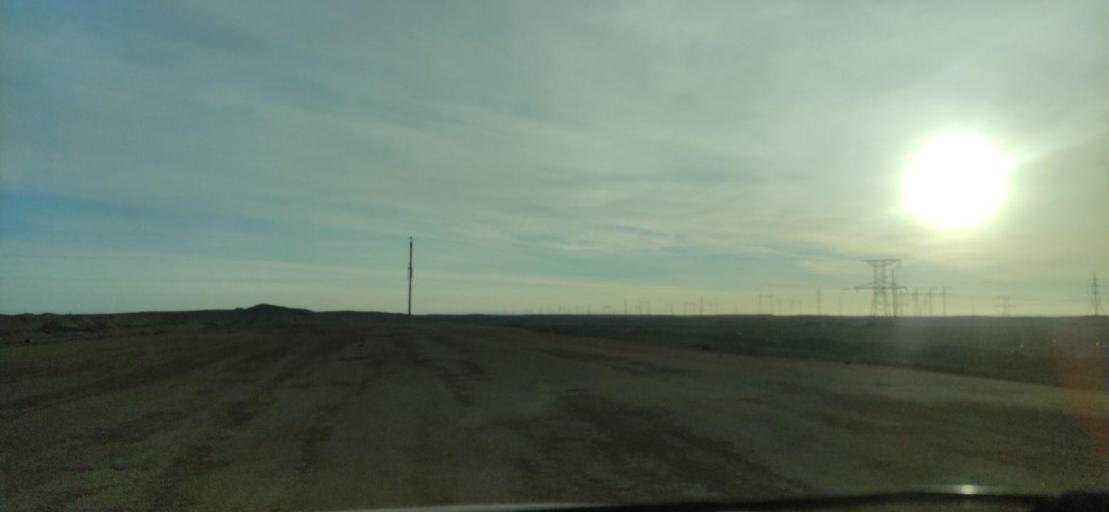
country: KZ
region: Qaraghandy
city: Saryshaghan
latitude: 46.1223
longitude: 73.5954
